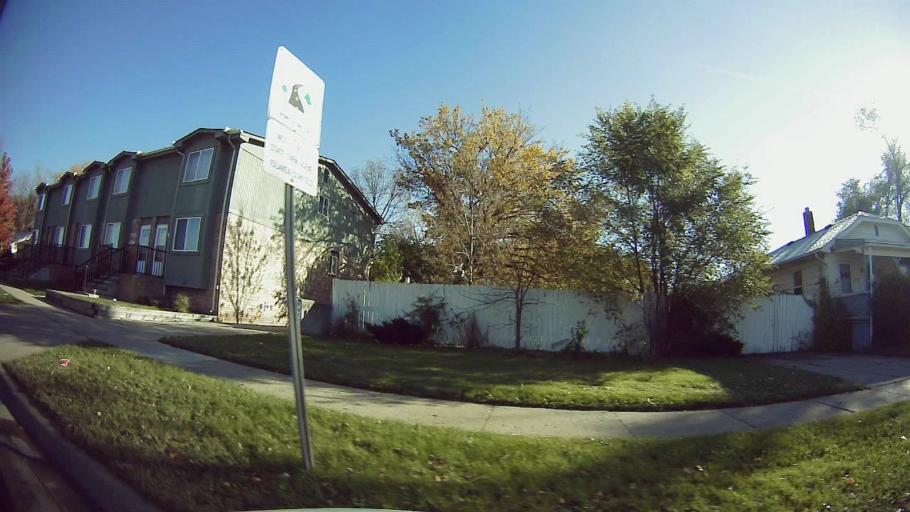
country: US
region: Michigan
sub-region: Oakland County
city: Berkley
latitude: 42.5037
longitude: -83.2030
